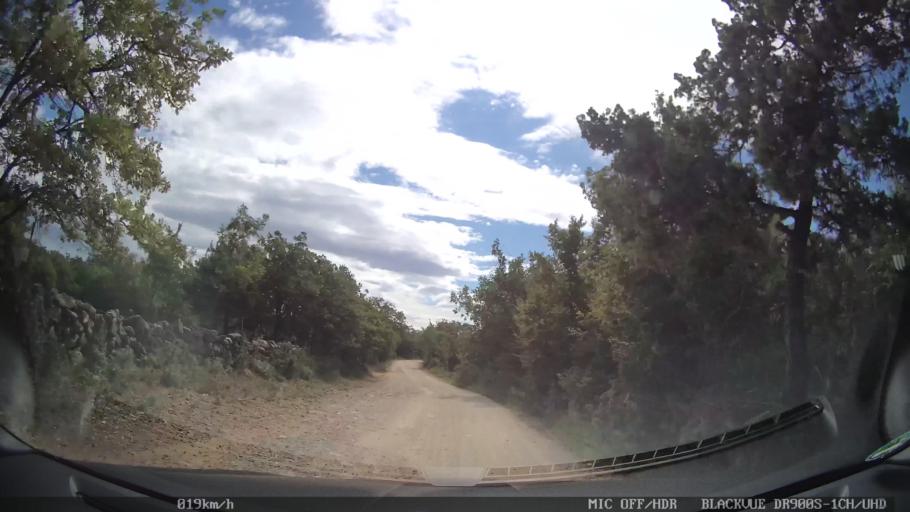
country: HR
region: Primorsko-Goranska
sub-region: Grad Krk
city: Krk
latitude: 45.0415
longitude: 14.5321
